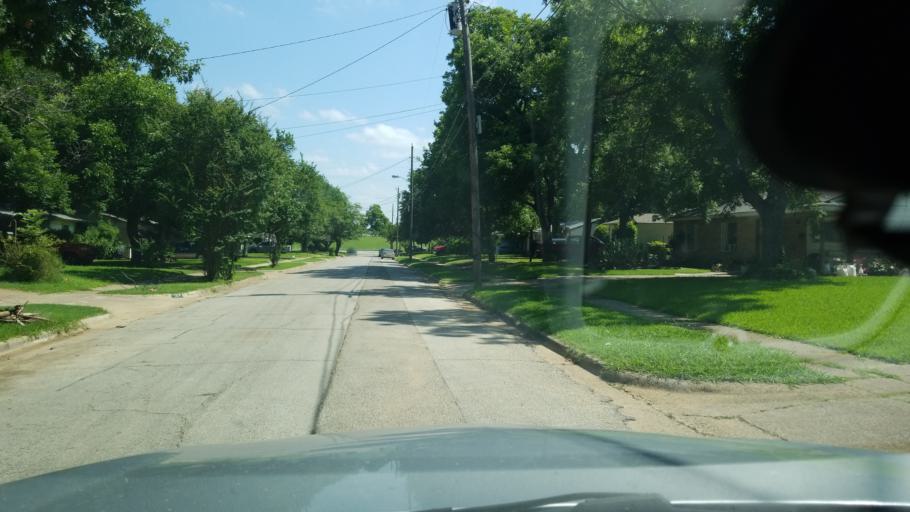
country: US
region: Texas
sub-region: Dallas County
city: Irving
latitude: 32.8184
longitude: -96.9608
